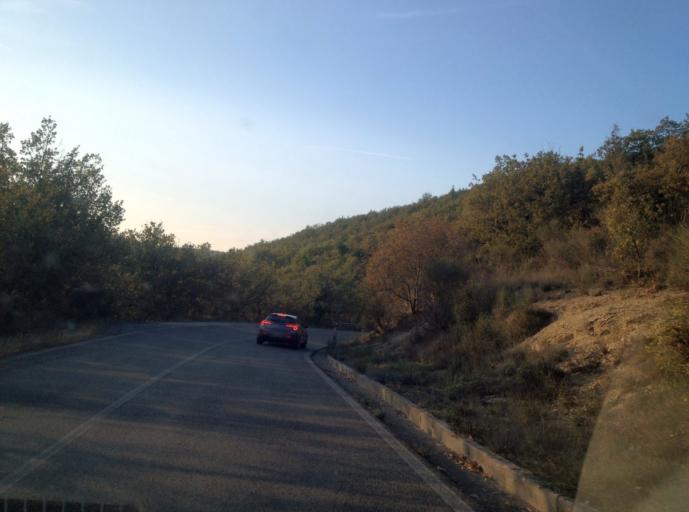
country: IT
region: Tuscany
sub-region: Provincia di Siena
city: Castellina in Chianti
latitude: 43.5023
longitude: 11.2995
